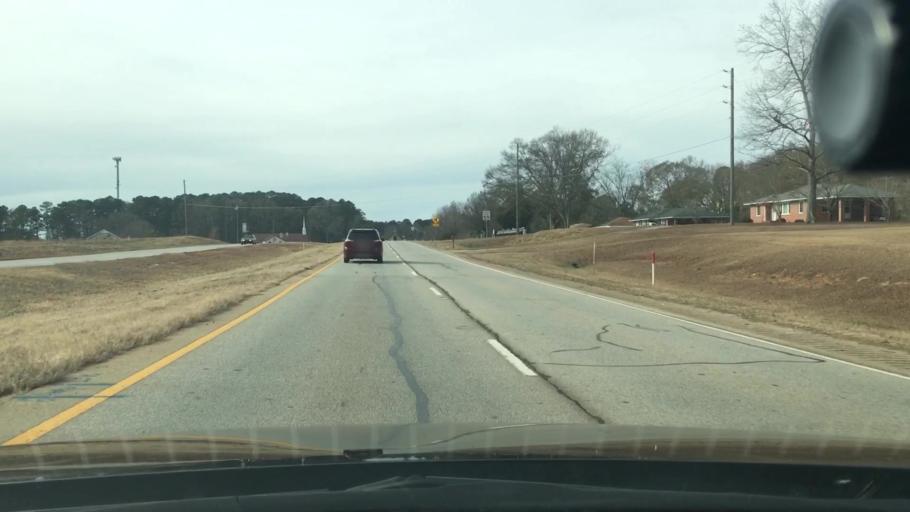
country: US
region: Georgia
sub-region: Spalding County
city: Experiment
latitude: 33.2739
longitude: -84.3101
